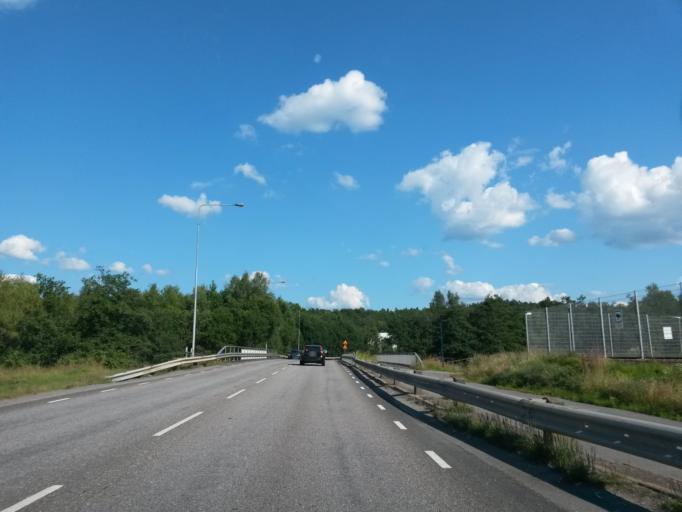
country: SE
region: Vaestra Goetaland
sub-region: Goteborg
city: Hammarkullen
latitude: 57.7878
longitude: 12.0464
